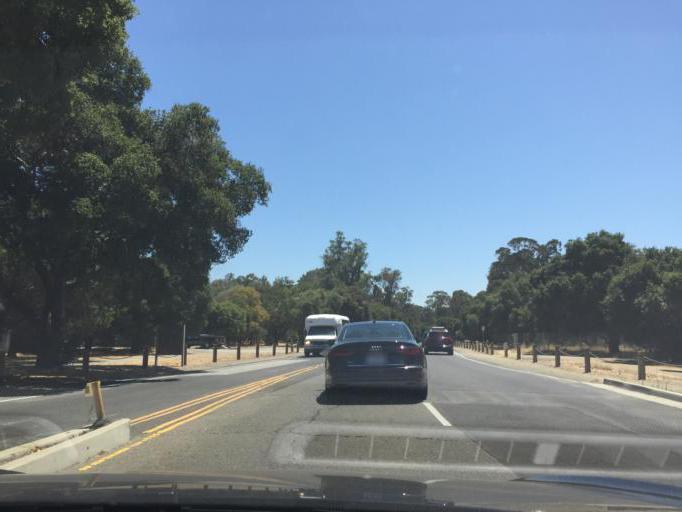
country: US
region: California
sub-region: Santa Clara County
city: Stanford
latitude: 37.4391
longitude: -122.1700
